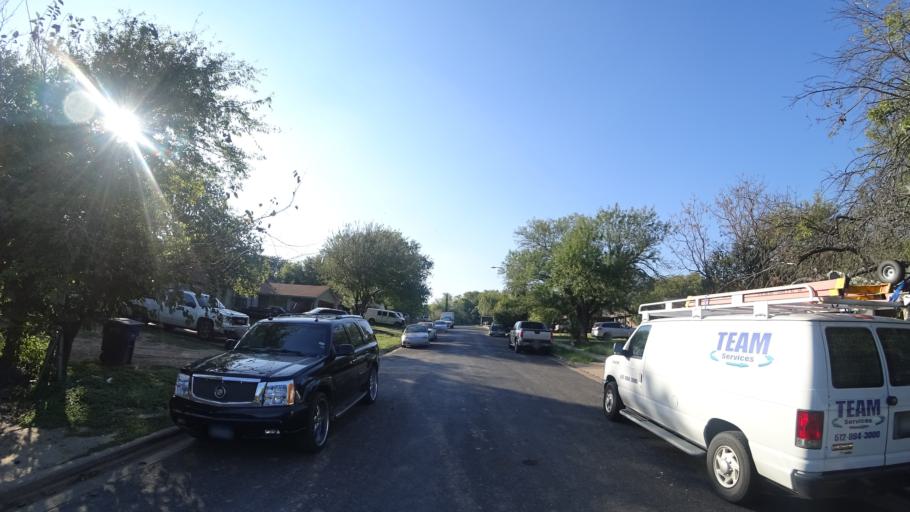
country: US
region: Texas
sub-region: Travis County
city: Wells Branch
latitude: 30.3563
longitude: -97.6778
